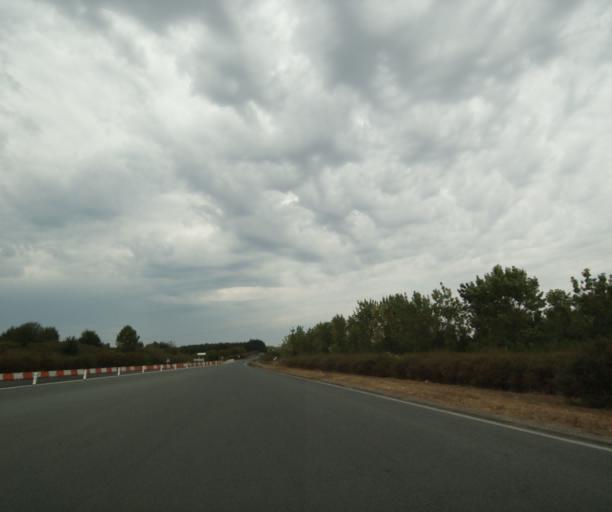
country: FR
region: Poitou-Charentes
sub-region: Departement de la Charente-Maritime
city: Tonnay-Charente
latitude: 45.9558
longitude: -0.8820
